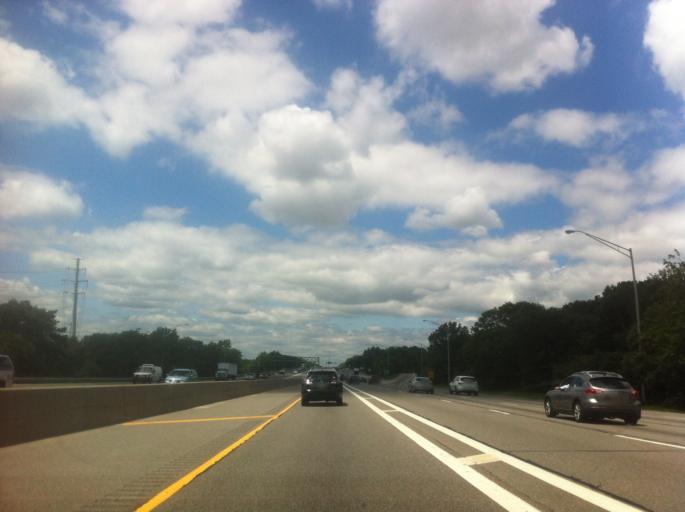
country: US
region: New York
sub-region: Suffolk County
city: Islandia
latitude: 40.8090
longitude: -73.1767
